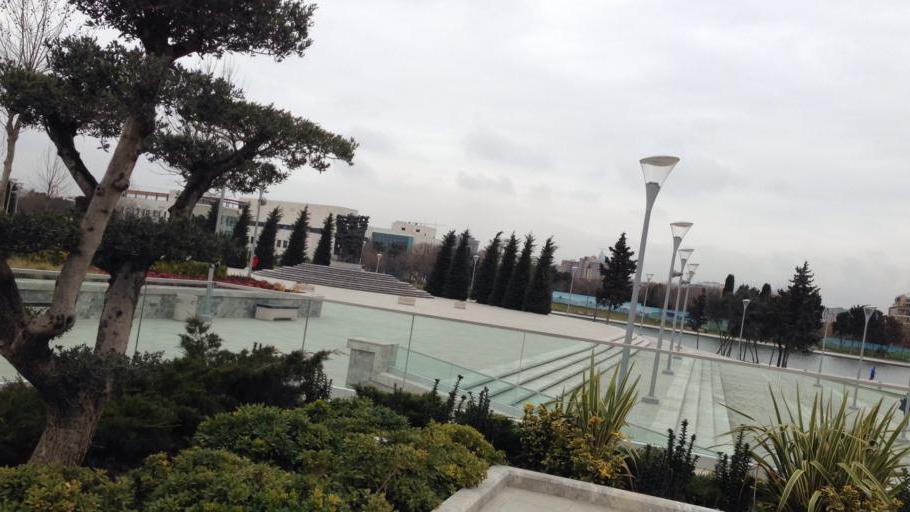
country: AZ
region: Baki
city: Baku
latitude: 40.3923
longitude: 49.8461
